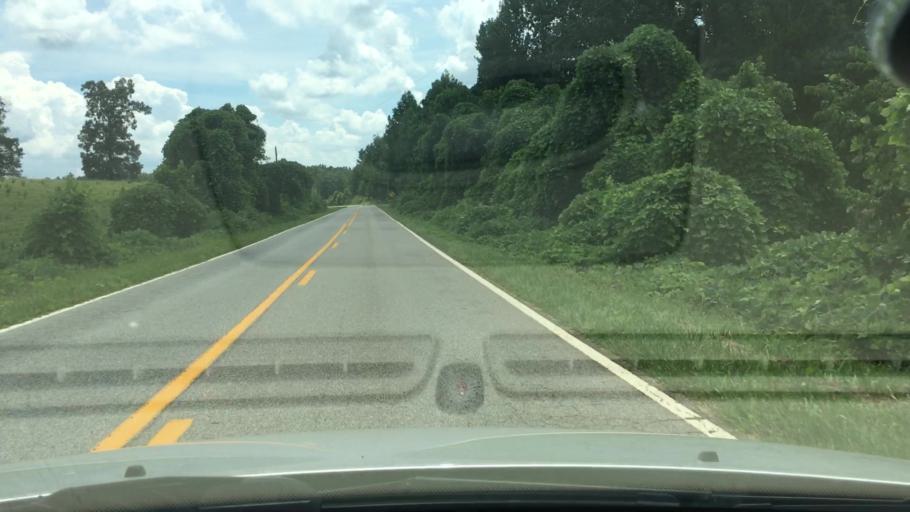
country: US
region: Georgia
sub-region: Lumpkin County
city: Dahlonega
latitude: 34.6004
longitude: -83.8959
